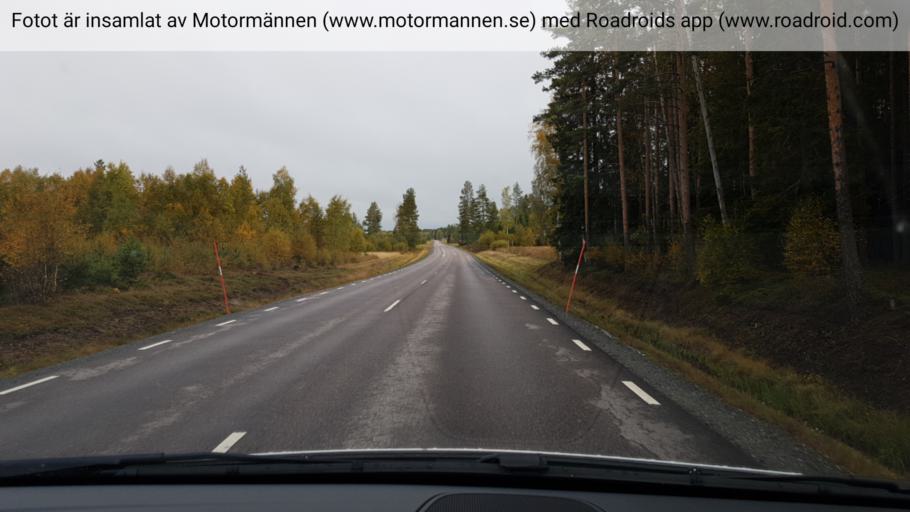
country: SE
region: Vaesterbotten
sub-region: Umea Kommun
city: Ersmark
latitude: 63.9072
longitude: 20.3127
